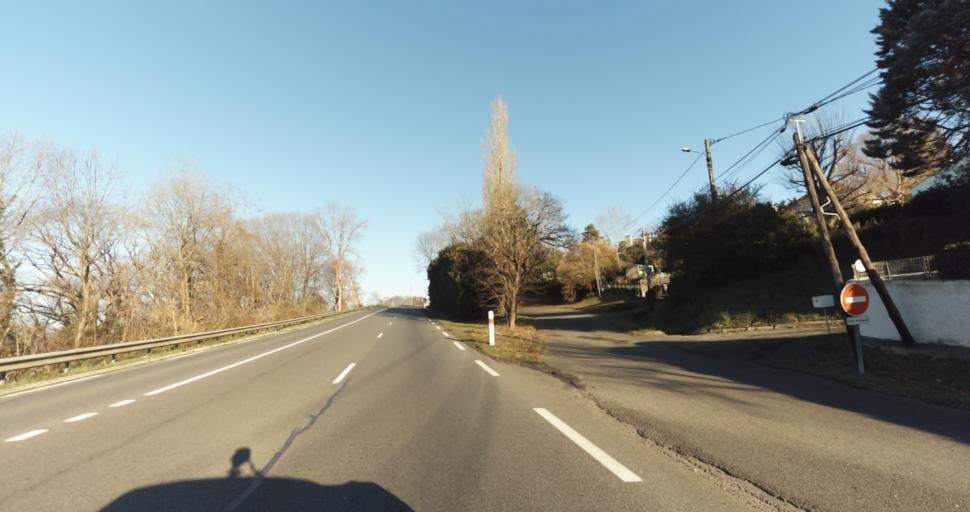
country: FR
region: Aquitaine
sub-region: Departement des Pyrenees-Atlantiques
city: Morlaas
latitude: 43.3322
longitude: -0.2775
